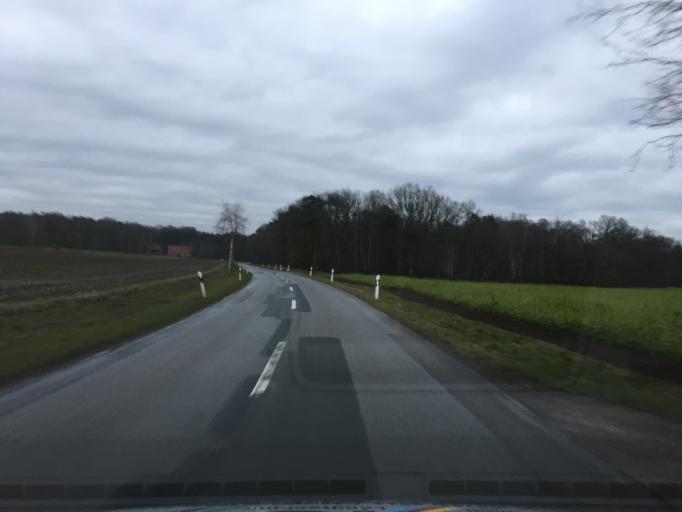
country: DE
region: Lower Saxony
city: Borstel
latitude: 52.6519
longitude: 8.9901
